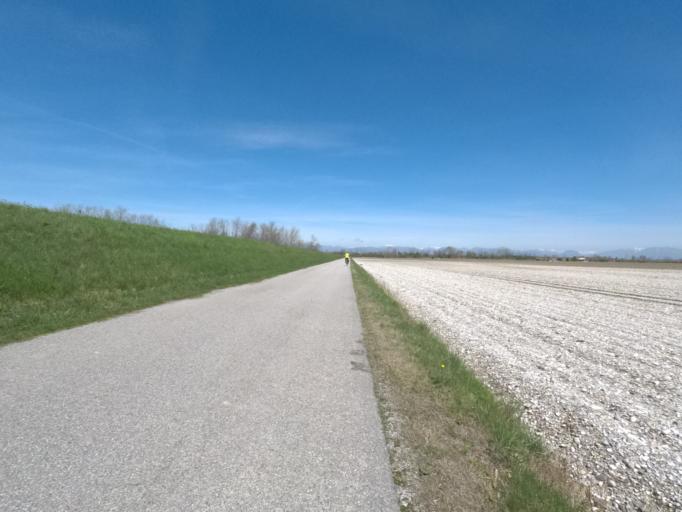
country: IT
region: Friuli Venezia Giulia
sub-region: Provincia di Udine
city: Camino al Tagliamento
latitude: 45.9538
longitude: 12.9142
